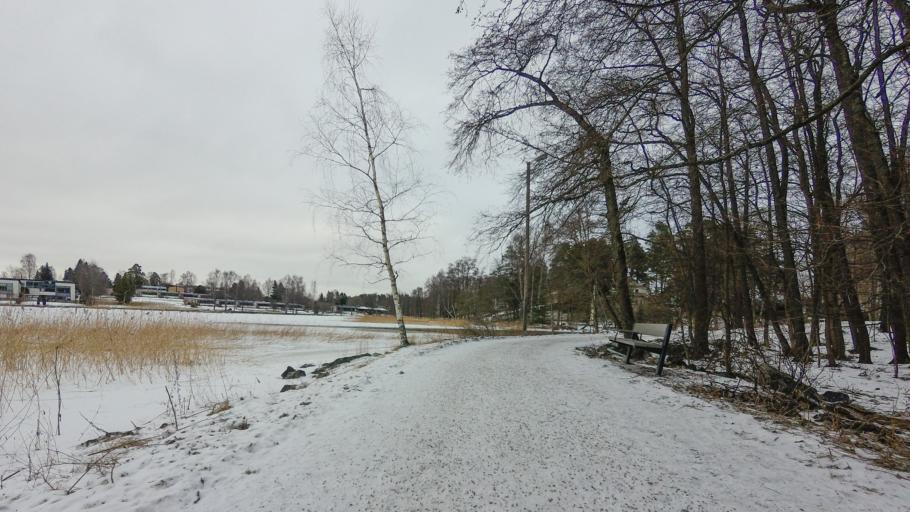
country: FI
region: Uusimaa
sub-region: Helsinki
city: Vantaa
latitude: 60.1878
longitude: 25.0565
